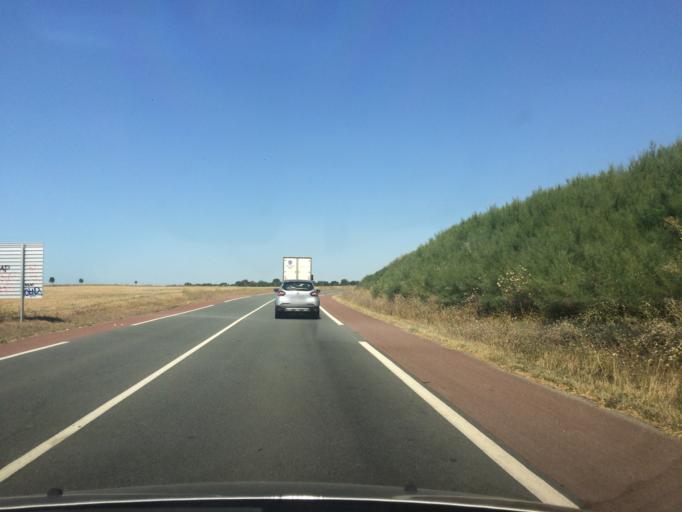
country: FR
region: Poitou-Charentes
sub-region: Departement de la Charente-Maritime
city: Saint-Xandre
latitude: 46.2355
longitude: -1.0757
